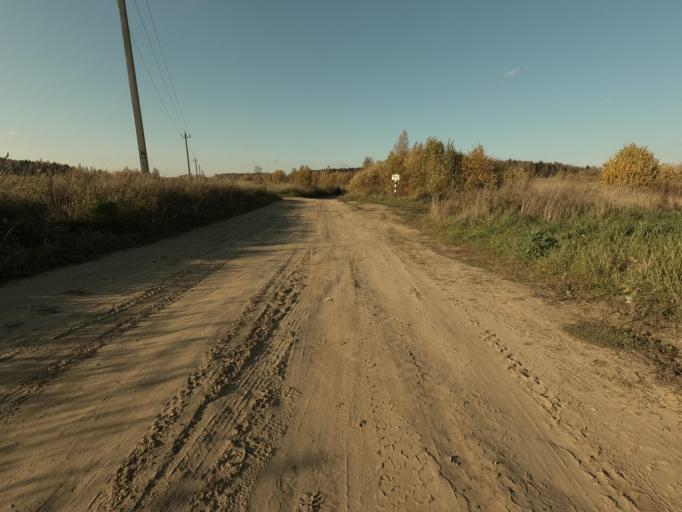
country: RU
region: Leningrad
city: Luppolovo
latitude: 60.1408
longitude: 30.2523
